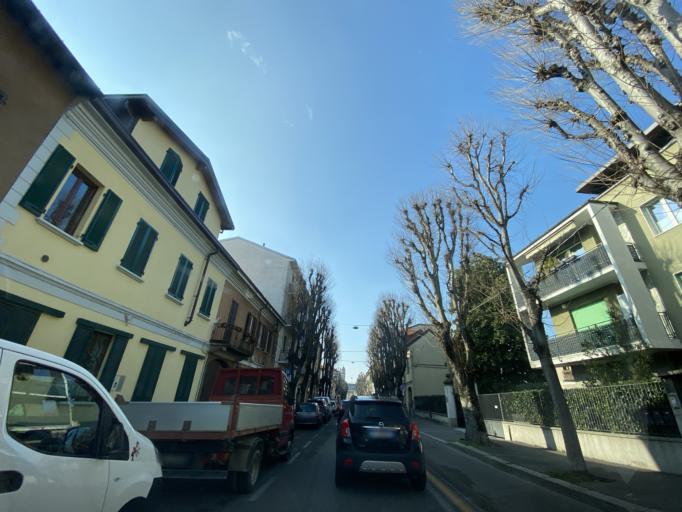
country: IT
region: Lombardy
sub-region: Provincia di Varese
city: Saronno
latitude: 45.6248
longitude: 9.0429
